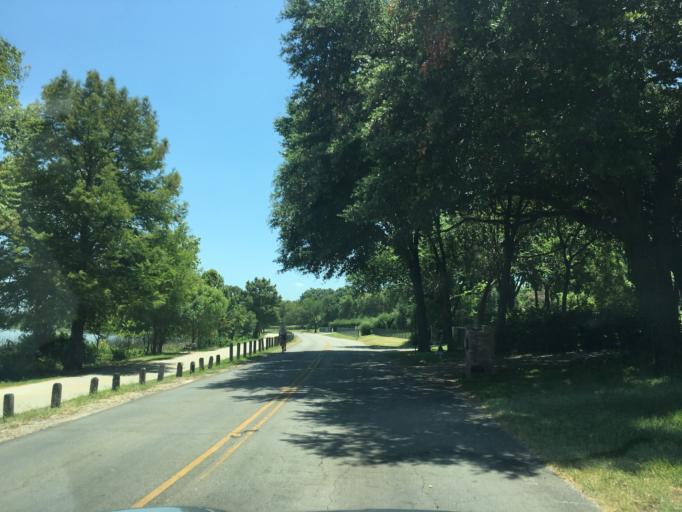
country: US
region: Texas
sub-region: Dallas County
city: Highland Park
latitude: 32.8395
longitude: -96.7294
